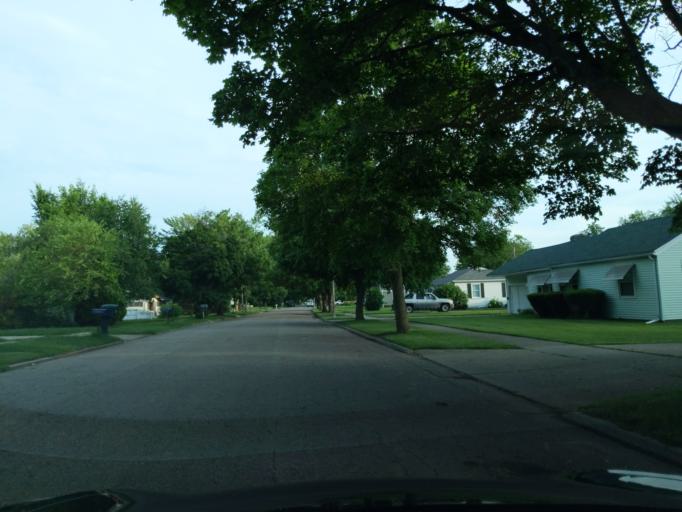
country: US
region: Michigan
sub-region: Ingham County
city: Edgemont Park
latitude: 42.7005
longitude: -84.5904
